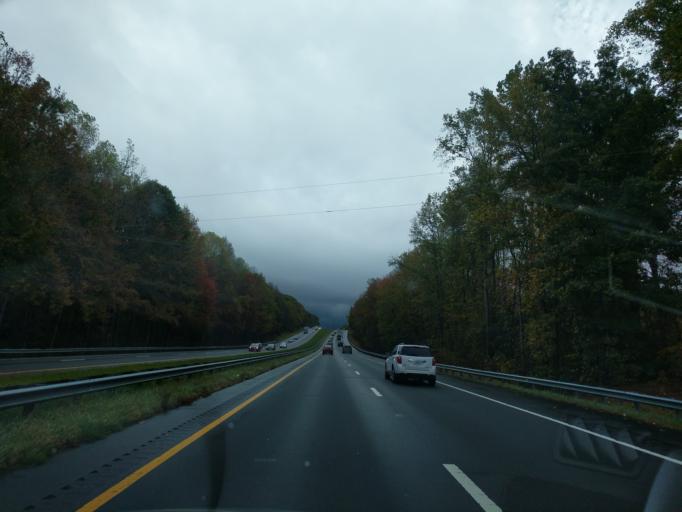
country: US
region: North Carolina
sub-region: Orange County
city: Hillsborough
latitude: 36.0493
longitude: -79.0545
